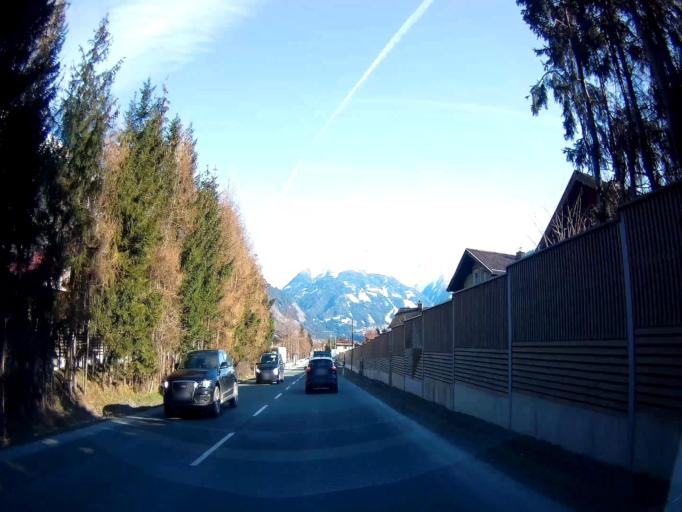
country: AT
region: Salzburg
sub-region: Politischer Bezirk Sankt Johann im Pongau
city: Bad Hofgastein
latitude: 47.1601
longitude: 13.1039
